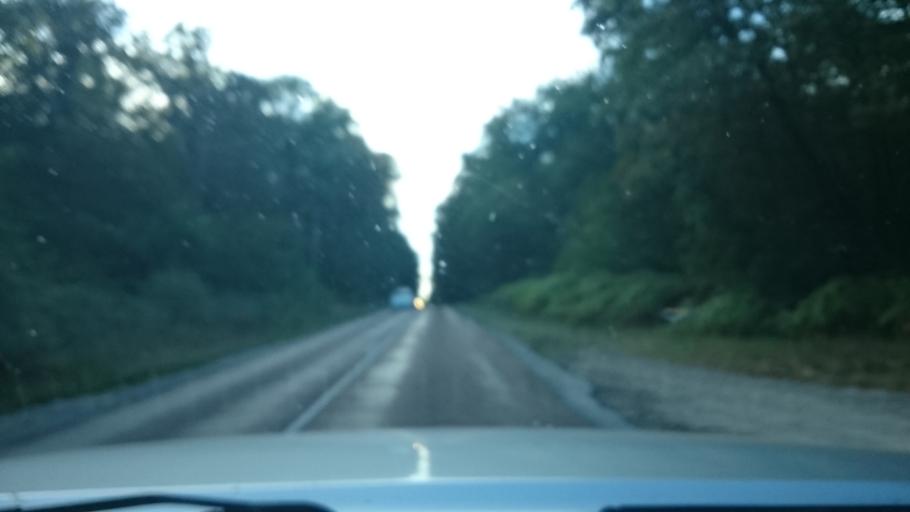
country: FR
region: Ile-de-France
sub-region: Departement de Seine-et-Marne
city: Samoreau
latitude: 48.4021
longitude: 2.7570
